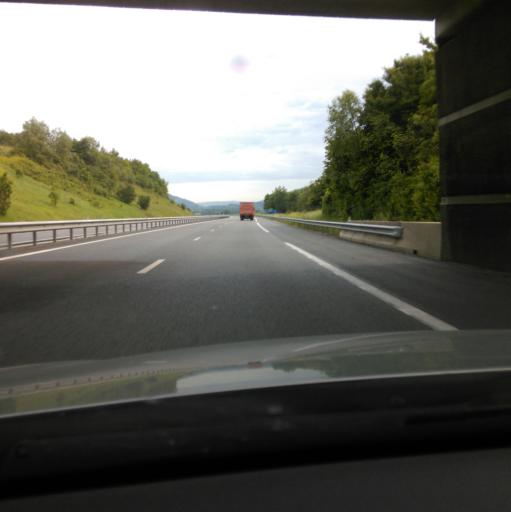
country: FR
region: Rhone-Alpes
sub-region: Departement de l'Ain
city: Saint-Martin-du-Frene
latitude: 46.1448
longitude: 5.5434
